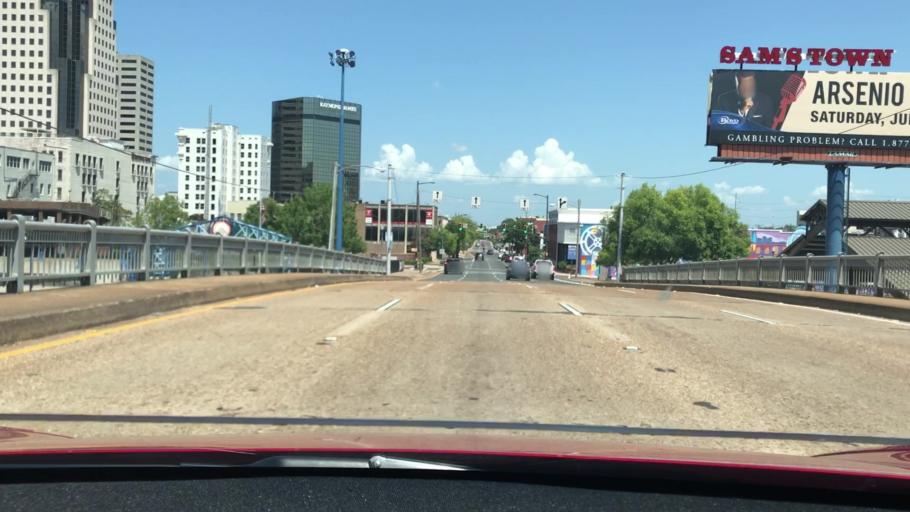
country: US
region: Louisiana
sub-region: Bossier Parish
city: Bossier City
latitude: 32.5126
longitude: -93.7444
